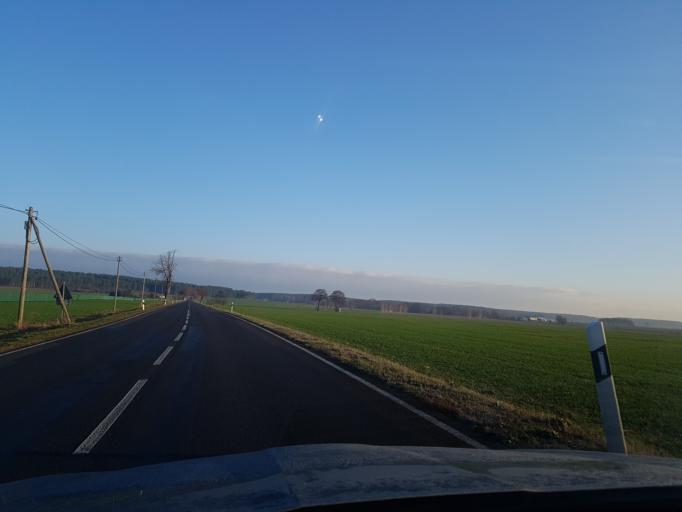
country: DE
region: Brandenburg
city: Schlieben
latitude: 51.7298
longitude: 13.4210
